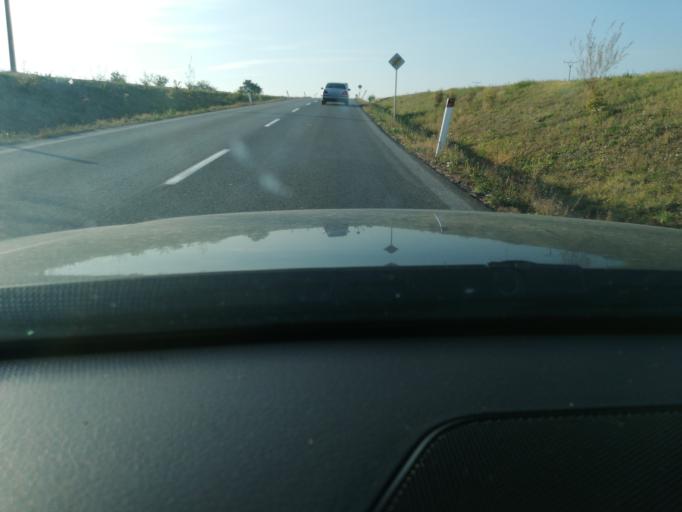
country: SK
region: Nitriansky
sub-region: Okres Nitra
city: Nitra
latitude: 48.3128
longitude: 18.0102
